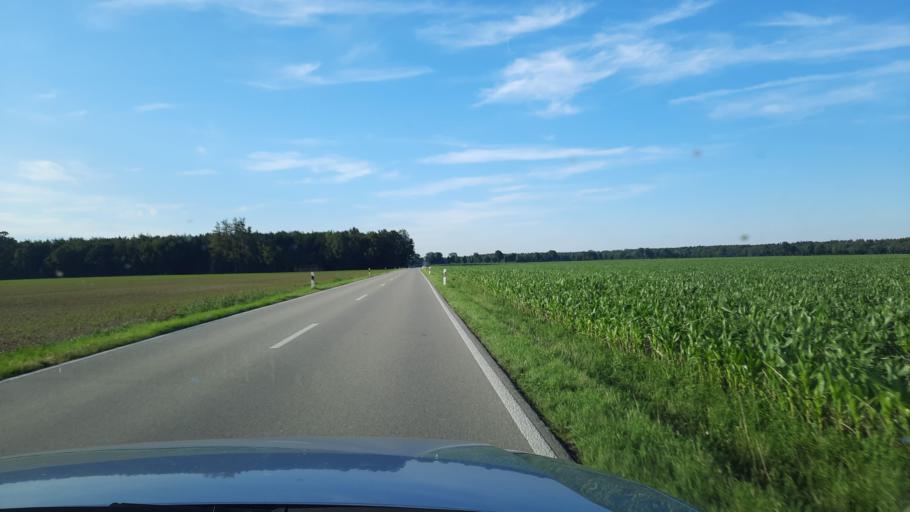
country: DE
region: Bavaria
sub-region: Upper Bavaria
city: Grasbrunn
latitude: 48.0640
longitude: 11.7730
